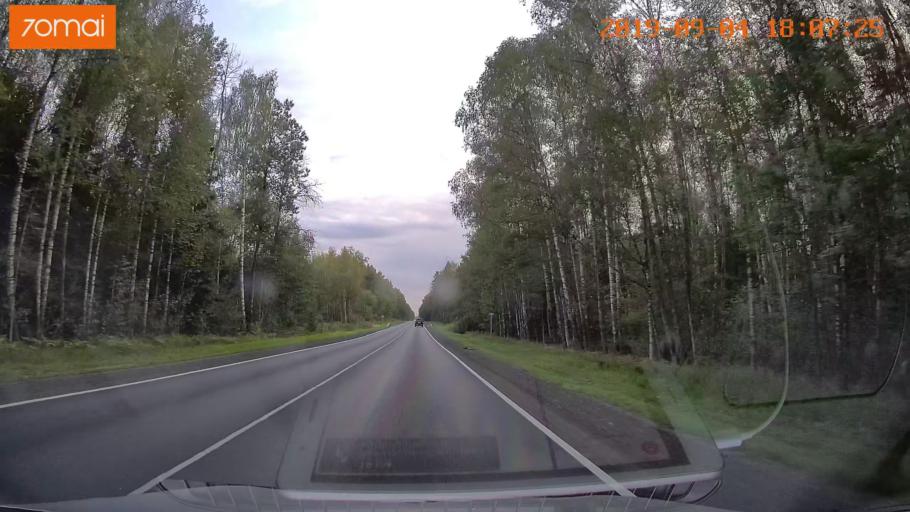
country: RU
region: Moskovskaya
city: Khorlovo
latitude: 55.4191
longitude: 38.8010
